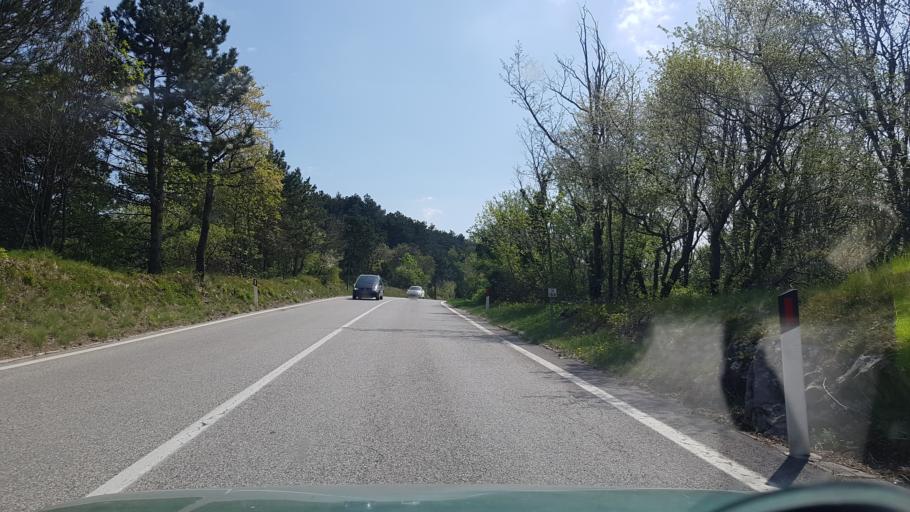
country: IT
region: Friuli Venezia Giulia
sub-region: Provincia di Trieste
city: Dolina
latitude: 45.6317
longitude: 13.8880
